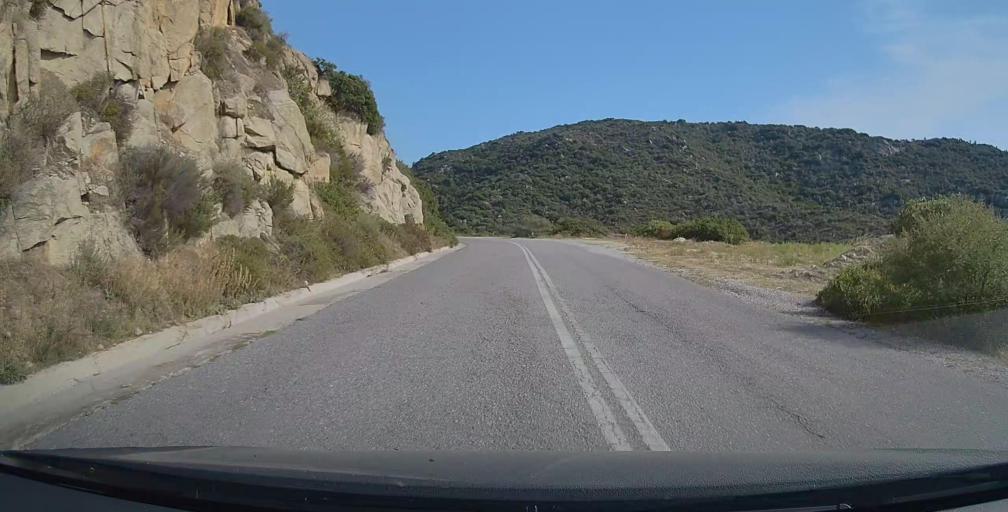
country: GR
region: Central Macedonia
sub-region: Nomos Chalkidikis
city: Sykia
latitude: 39.9993
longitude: 23.9845
